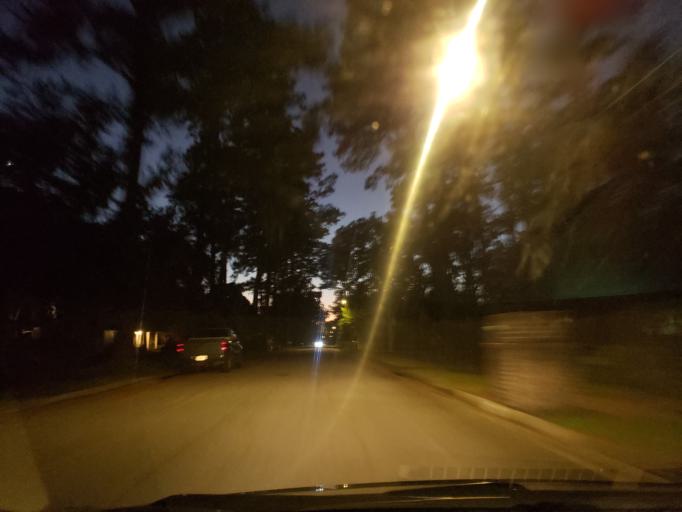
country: US
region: Georgia
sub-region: Chatham County
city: Isle of Hope
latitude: 31.9869
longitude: -81.0561
